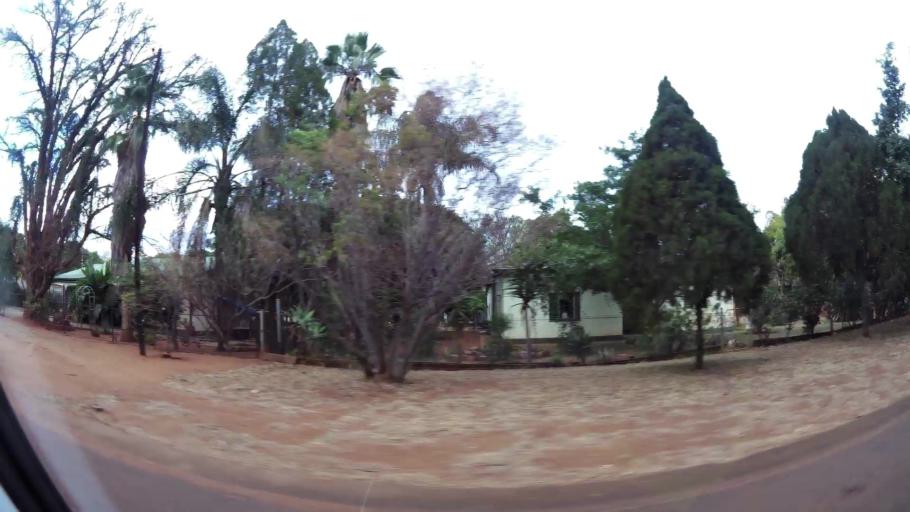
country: ZA
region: Limpopo
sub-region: Waterberg District Municipality
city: Modimolle
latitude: -24.5122
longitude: 28.7136
